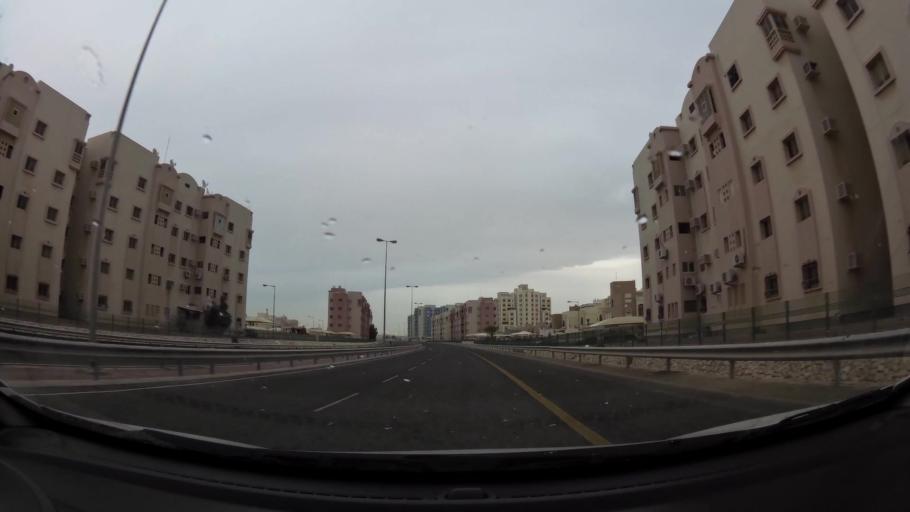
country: BH
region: Central Governorate
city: Madinat Hamad
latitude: 26.1190
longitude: 50.4881
